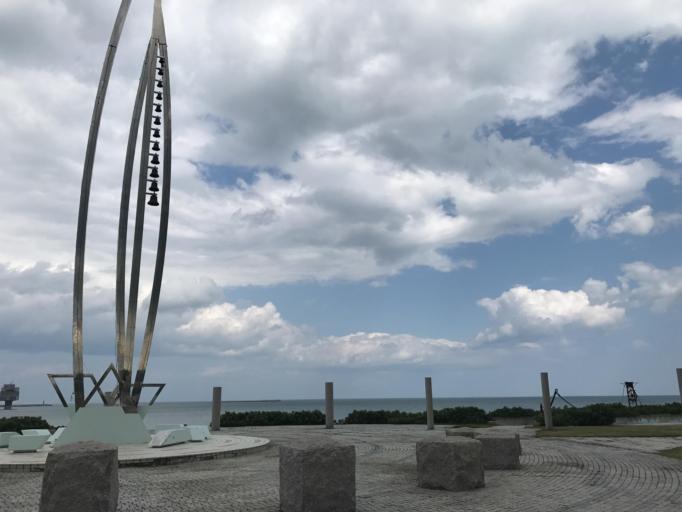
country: JP
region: Hokkaido
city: Mombetsu
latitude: 44.3292
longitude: 143.3751
